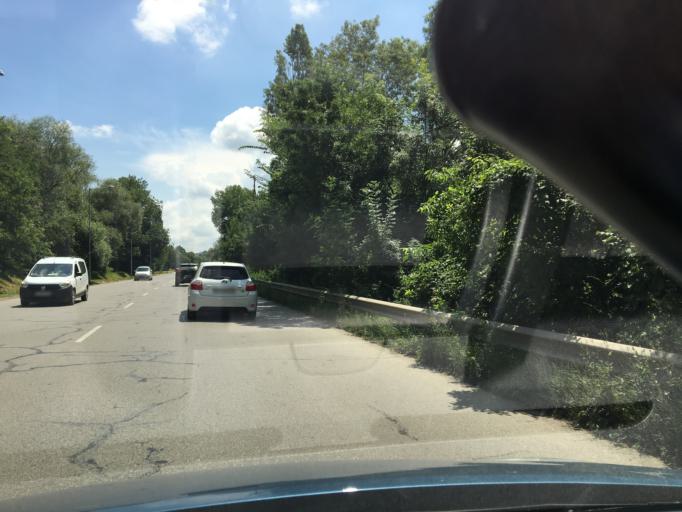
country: BG
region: Sofia-Capital
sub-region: Stolichna Obshtina
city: Sofia
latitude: 42.6619
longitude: 23.3041
